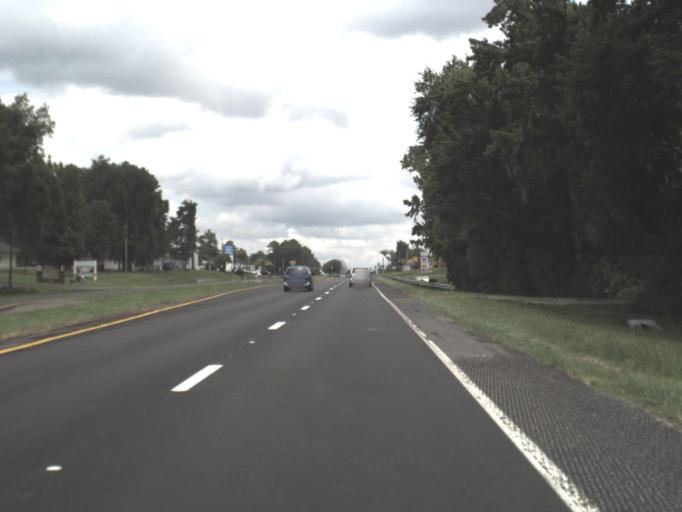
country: US
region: Florida
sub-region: Columbia County
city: Lake City
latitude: 30.1588
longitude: -82.6428
